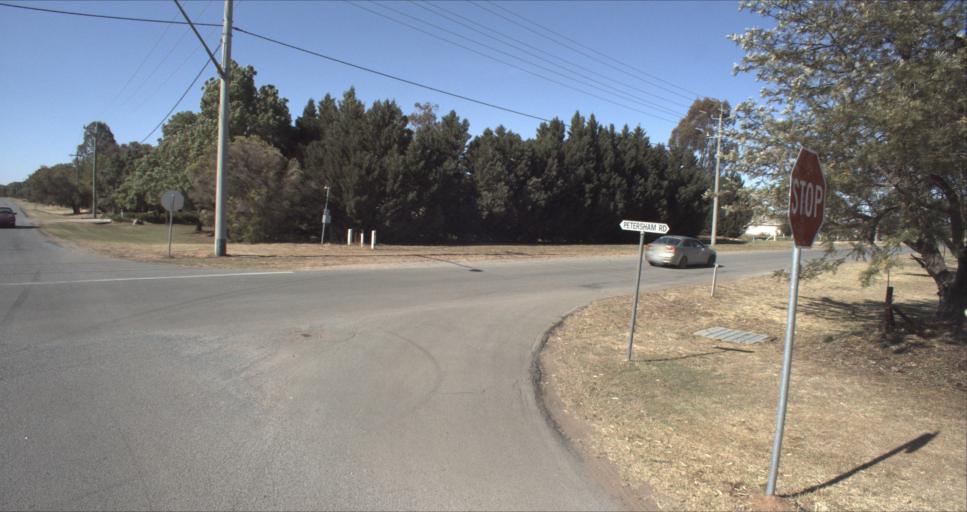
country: AU
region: New South Wales
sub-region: Leeton
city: Leeton
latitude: -34.5440
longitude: 146.4185
